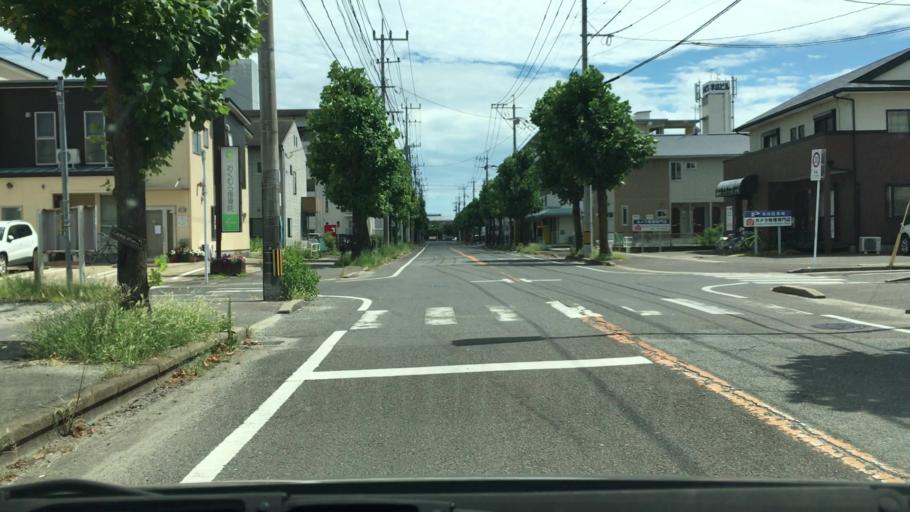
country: JP
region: Saga Prefecture
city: Saga-shi
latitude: 33.2688
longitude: 130.2870
